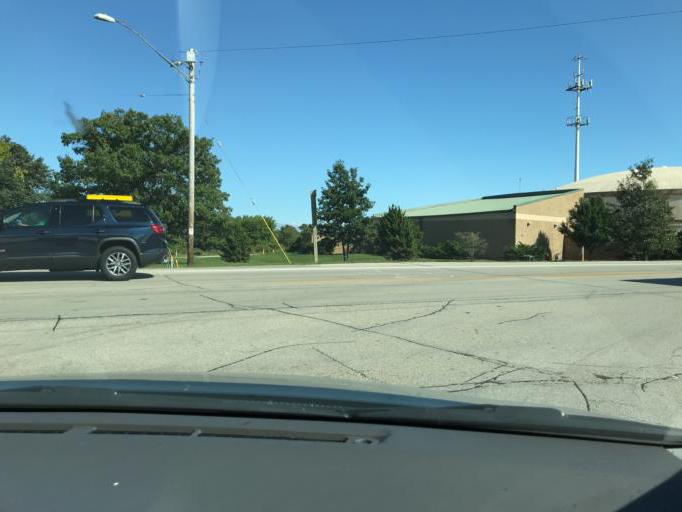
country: US
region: Illinois
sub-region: Lake County
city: Winthrop Harbor
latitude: 42.5220
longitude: -87.8242
